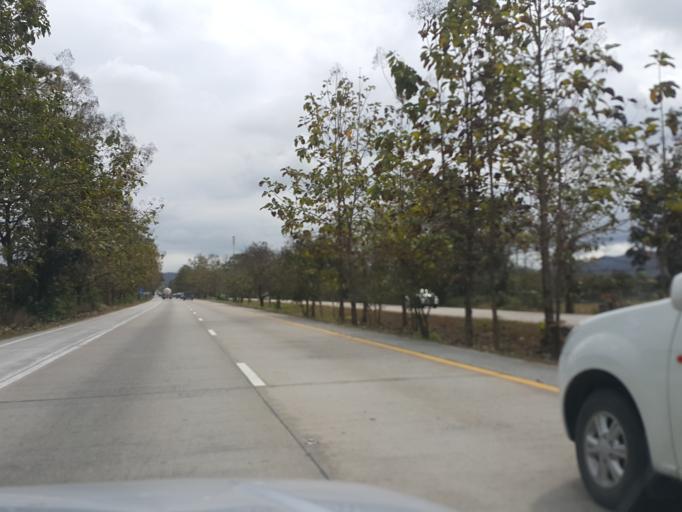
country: TH
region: Lamphun
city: Mae Tha
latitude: 18.5287
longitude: 99.0807
